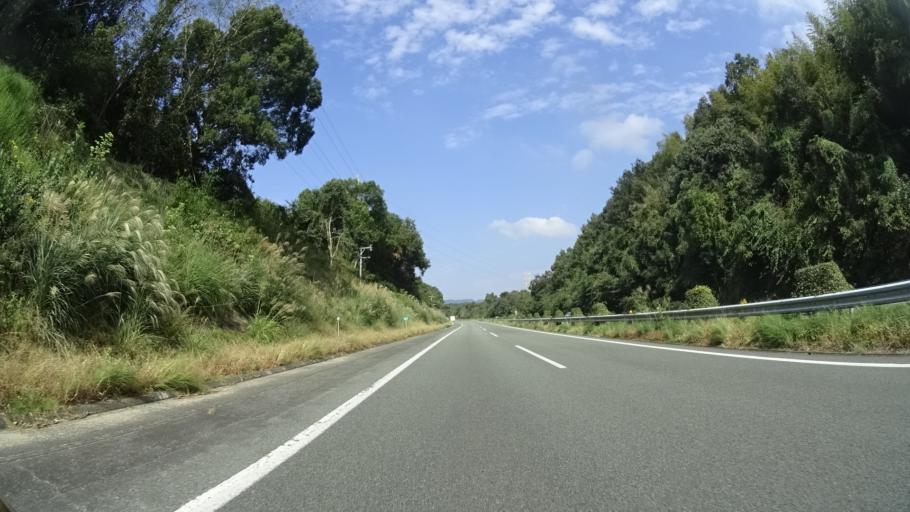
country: JP
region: Kumamoto
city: Matsubase
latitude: 32.6325
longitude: 130.7101
